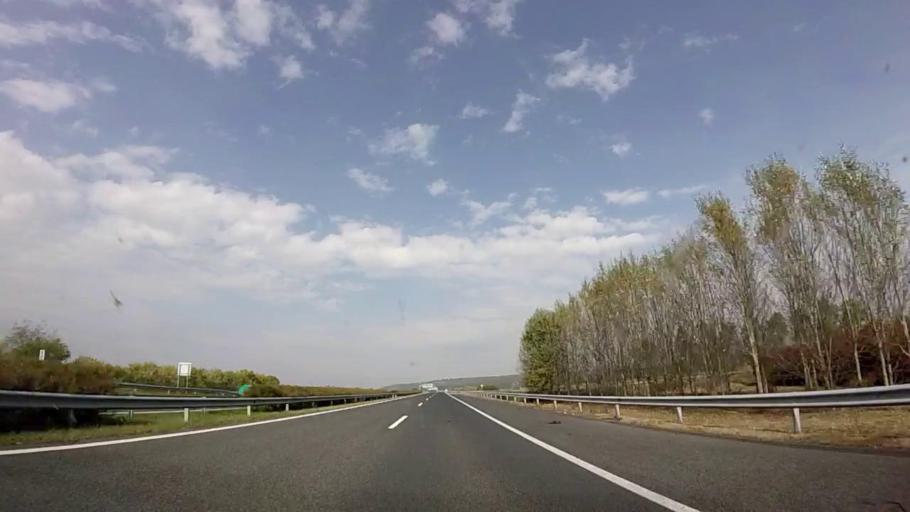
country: HU
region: Zala
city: Letenye
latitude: 46.4239
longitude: 16.7102
